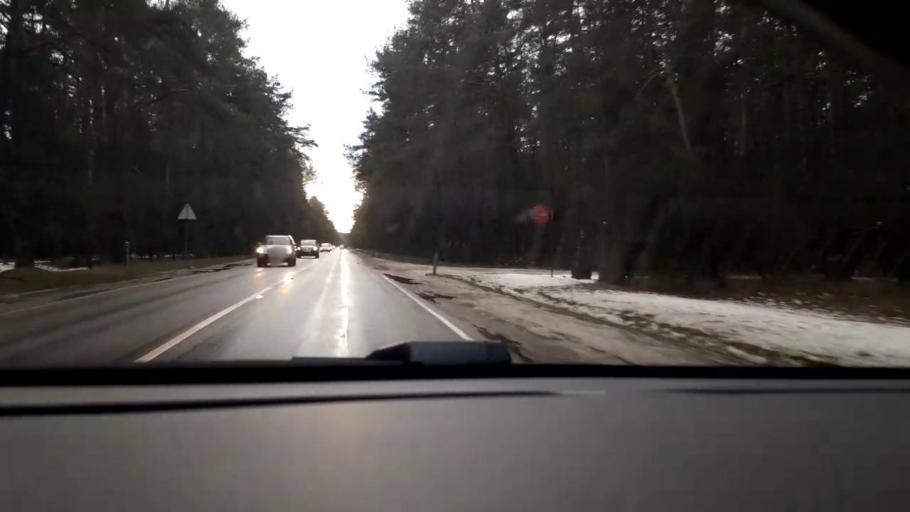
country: LT
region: Vilnius County
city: Rasos
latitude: 54.7713
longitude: 25.3815
